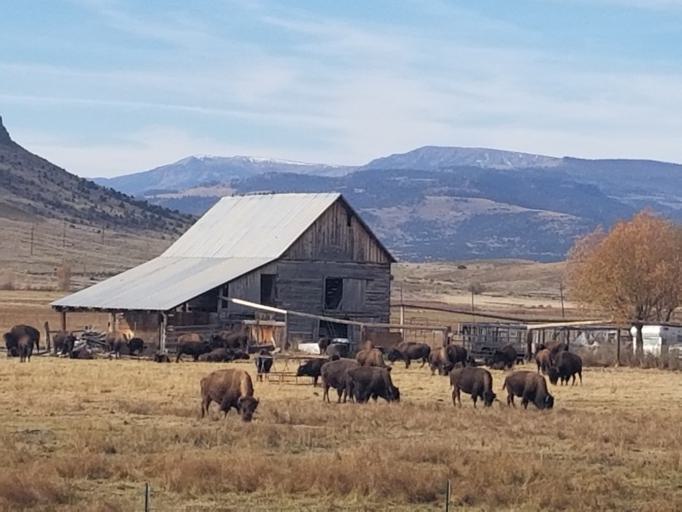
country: US
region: Colorado
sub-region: Rio Grande County
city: Del Norte
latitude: 37.6794
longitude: -106.3661
